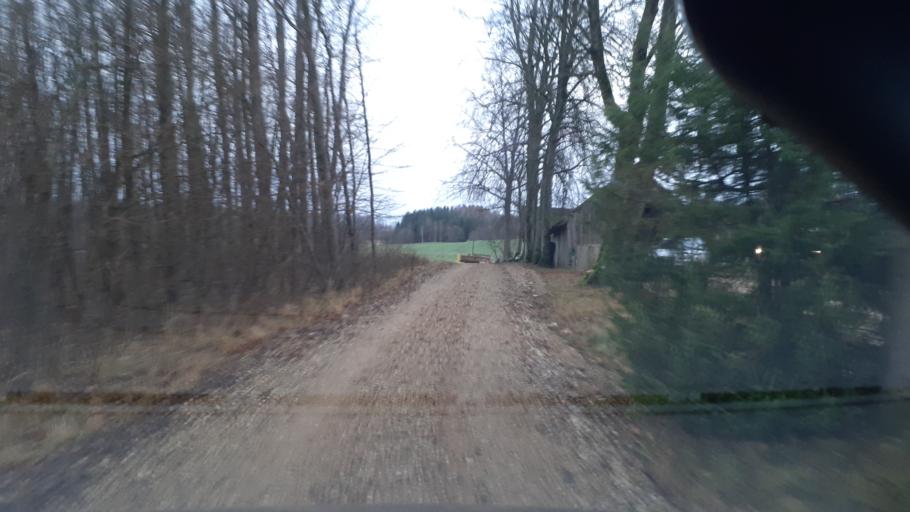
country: LV
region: Alsunga
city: Alsunga
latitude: 56.8788
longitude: 21.6859
